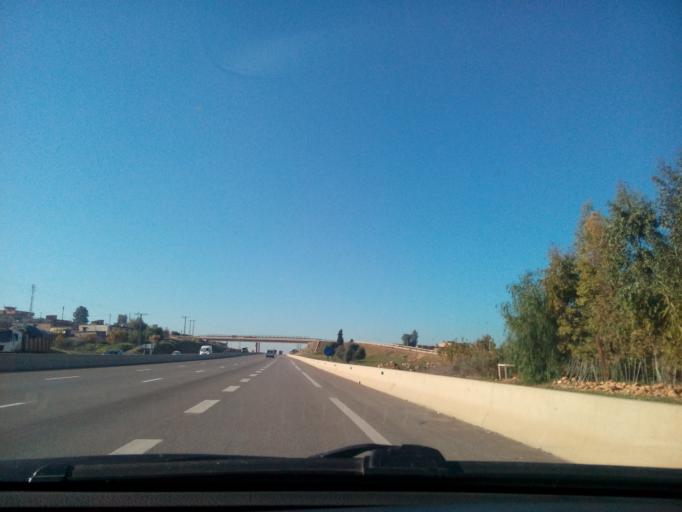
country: DZ
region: Chlef
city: Boukadir
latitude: 36.0544
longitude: 1.1365
